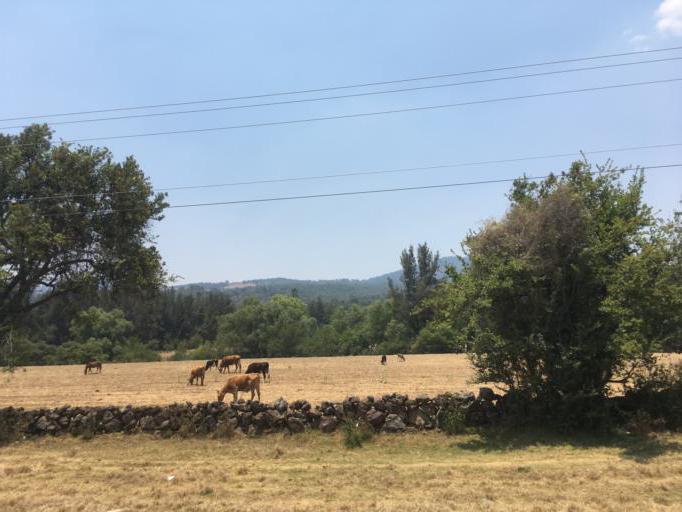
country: MX
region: Michoacan
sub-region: Morelia
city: Iratzio
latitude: 19.6291
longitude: -101.4650
